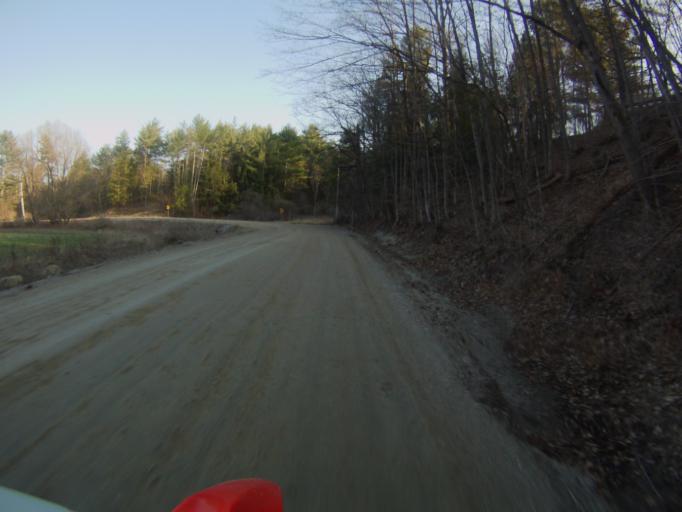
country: US
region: Vermont
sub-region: Addison County
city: Bristol
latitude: 44.0914
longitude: -73.1035
